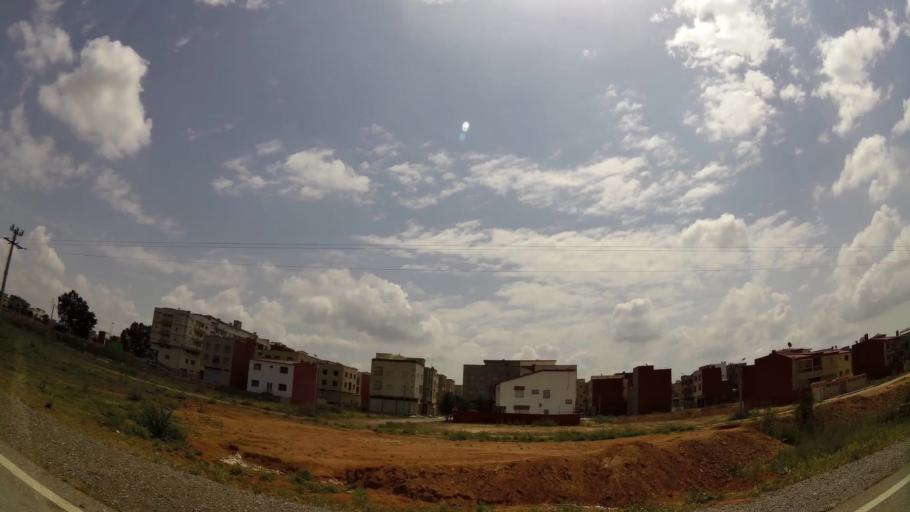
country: MA
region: Gharb-Chrarda-Beni Hssen
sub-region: Kenitra Province
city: Kenitra
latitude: 34.0118
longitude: -6.5403
